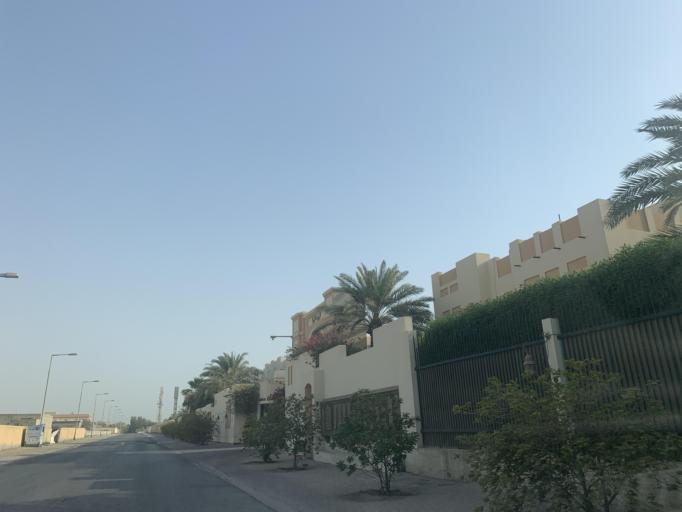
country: BH
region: Central Governorate
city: Madinat Hamad
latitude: 26.1788
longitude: 50.4677
